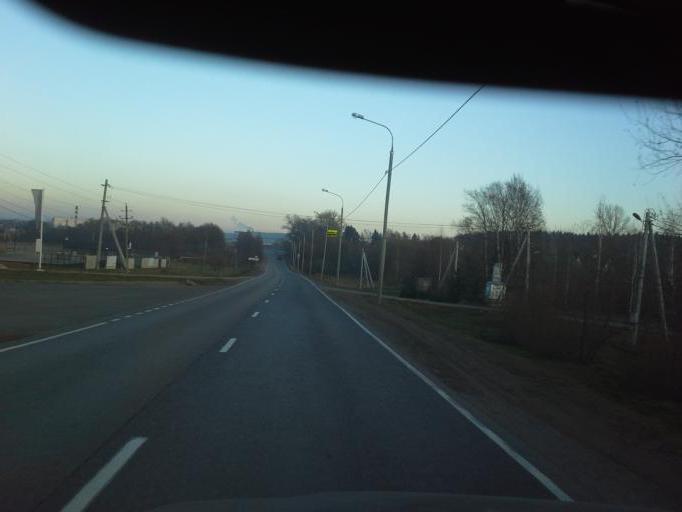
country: RU
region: Moskovskaya
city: Kokoshkino
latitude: 55.5794
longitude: 37.1553
